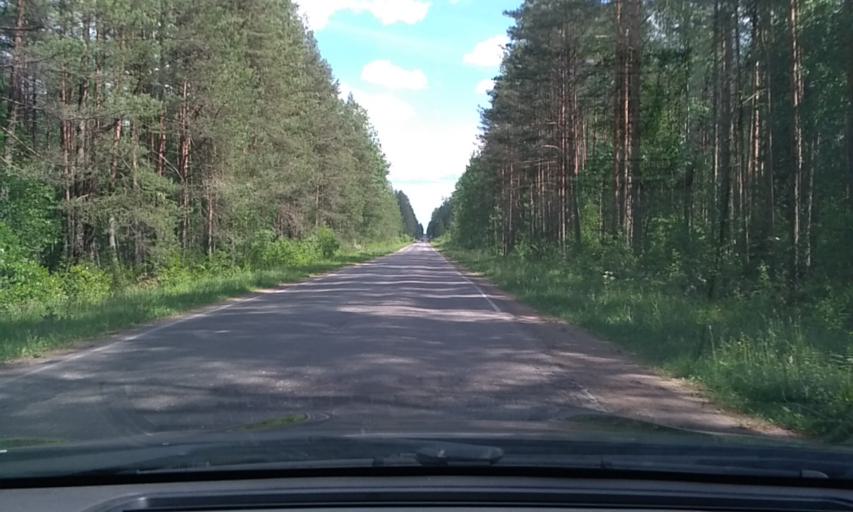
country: RU
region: Leningrad
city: Imeni Sverdlova
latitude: 59.8238
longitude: 30.7283
